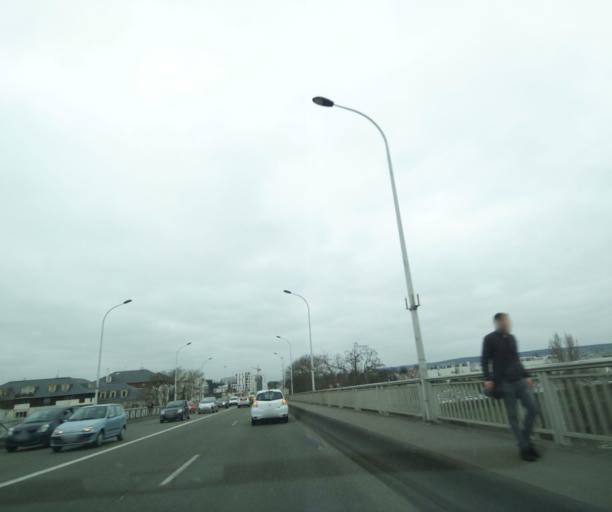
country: FR
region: Ile-de-France
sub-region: Departement des Yvelines
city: Carrieres-sous-Poissy
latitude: 48.9368
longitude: 2.0388
